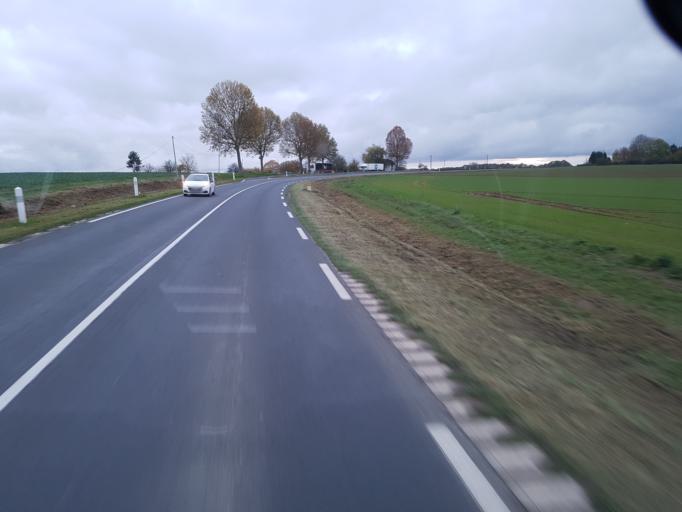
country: FR
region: Champagne-Ardenne
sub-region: Departement de la Marne
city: Montmirail
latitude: 48.8823
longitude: 3.5214
